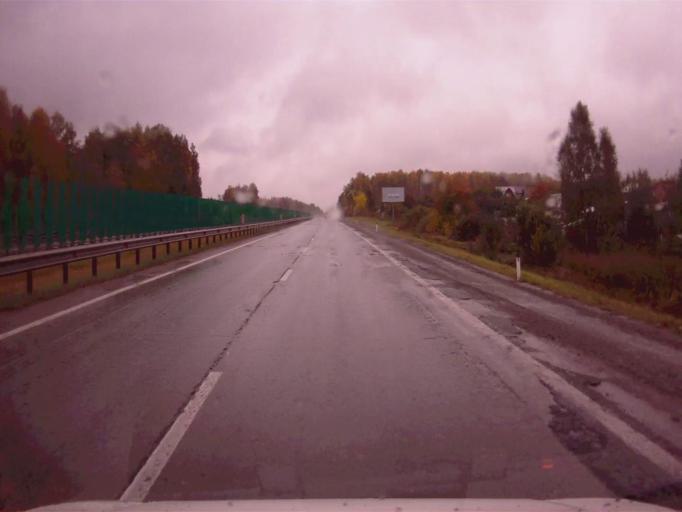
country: RU
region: Chelyabinsk
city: Dolgoderevenskoye
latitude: 55.3297
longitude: 61.3223
